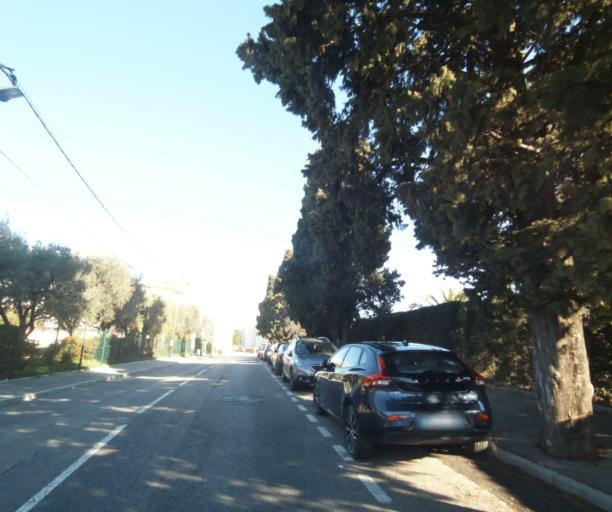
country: FR
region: Provence-Alpes-Cote d'Azur
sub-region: Departement des Alpes-Maritimes
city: Antibes
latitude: 43.5853
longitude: 7.1013
